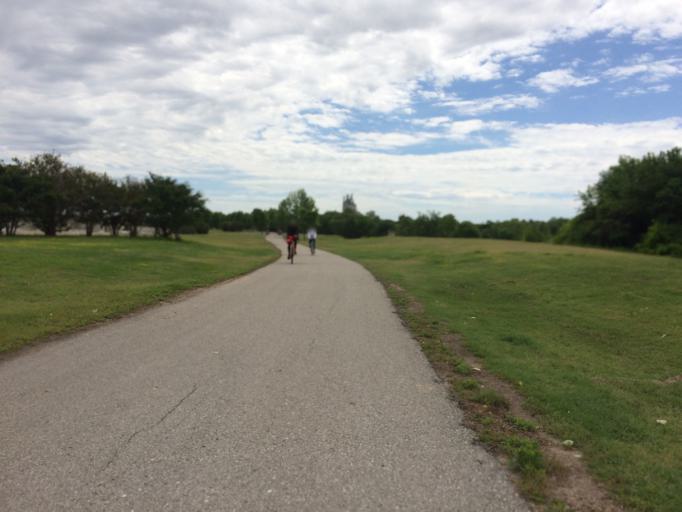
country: US
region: Oklahoma
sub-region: Oklahoma County
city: Oklahoma City
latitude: 35.4484
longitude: -97.5257
